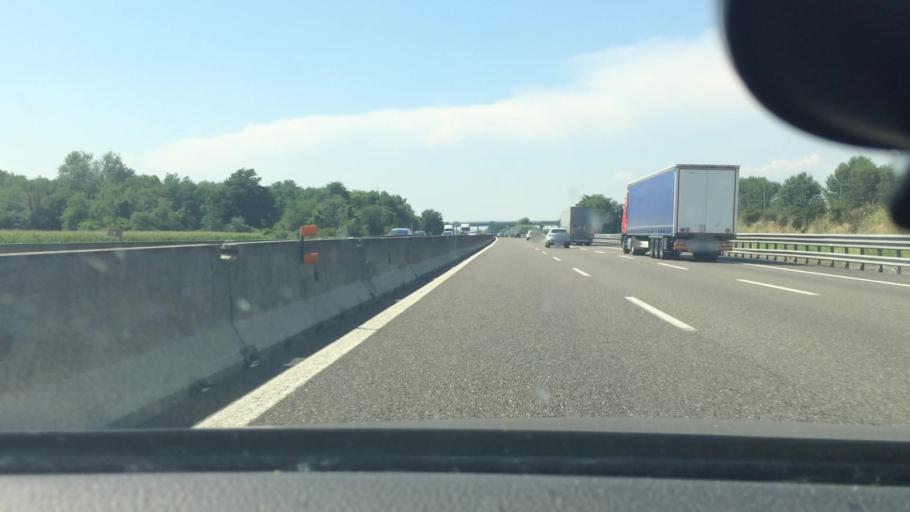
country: IT
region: Lombardy
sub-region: Provincia di Lodi
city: Lodi Vecchio
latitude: 45.3024
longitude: 9.4052
